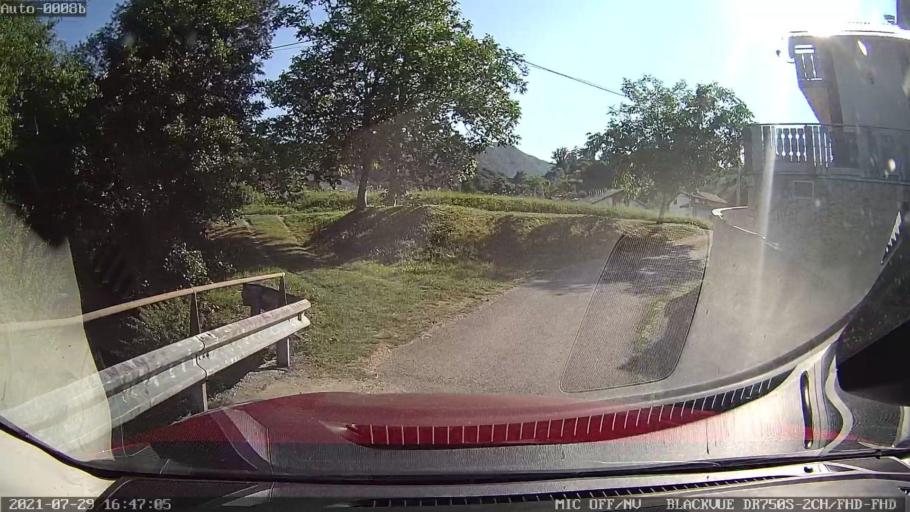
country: HR
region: Varazdinska
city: Ivanec
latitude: 46.2171
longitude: 16.1270
